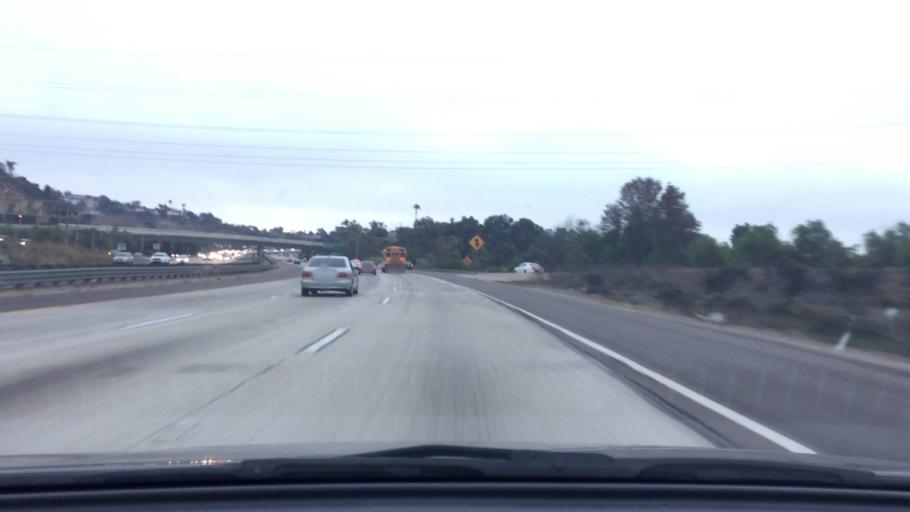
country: US
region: California
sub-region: San Diego County
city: Chula Vista
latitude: 32.6587
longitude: -117.0719
